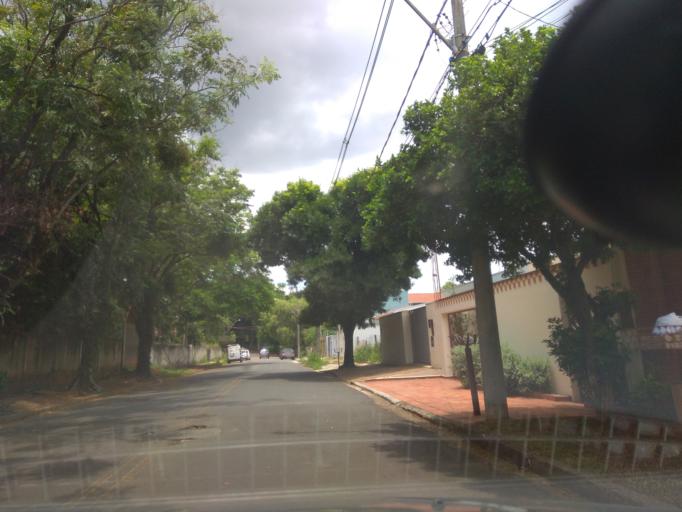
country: BR
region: Sao Paulo
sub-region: Campinas
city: Campinas
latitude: -22.8249
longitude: -47.0778
